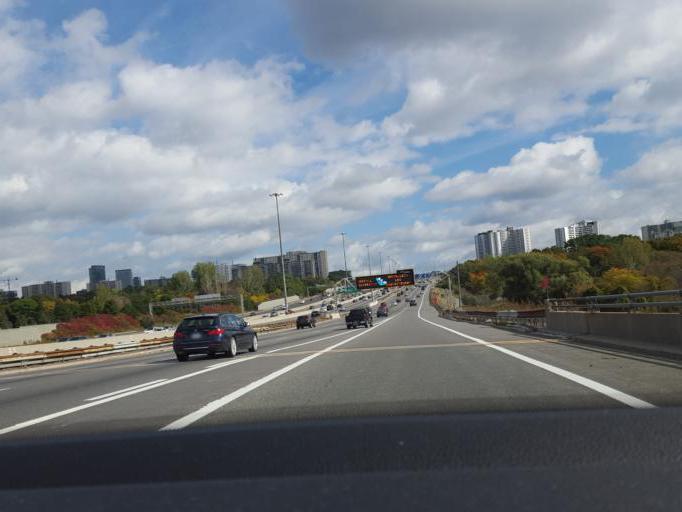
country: CA
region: Ontario
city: Willowdale
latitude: 43.7661
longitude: -79.3592
